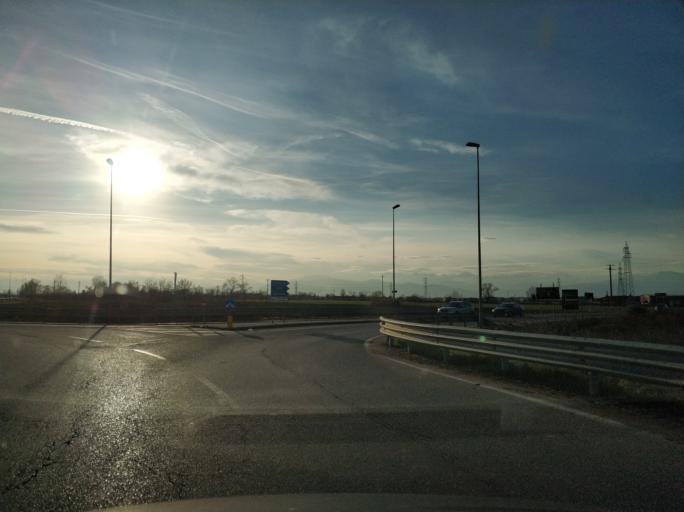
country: IT
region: Piedmont
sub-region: Provincia di Torino
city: Brandizzo
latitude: 45.1840
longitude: 7.8287
